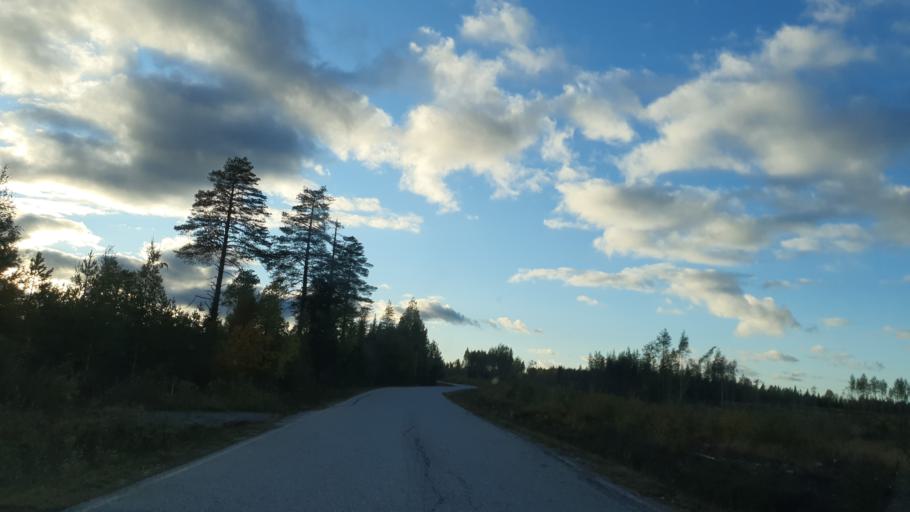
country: FI
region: Kainuu
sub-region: Kehys-Kainuu
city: Kuhmo
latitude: 63.9488
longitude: 29.7586
